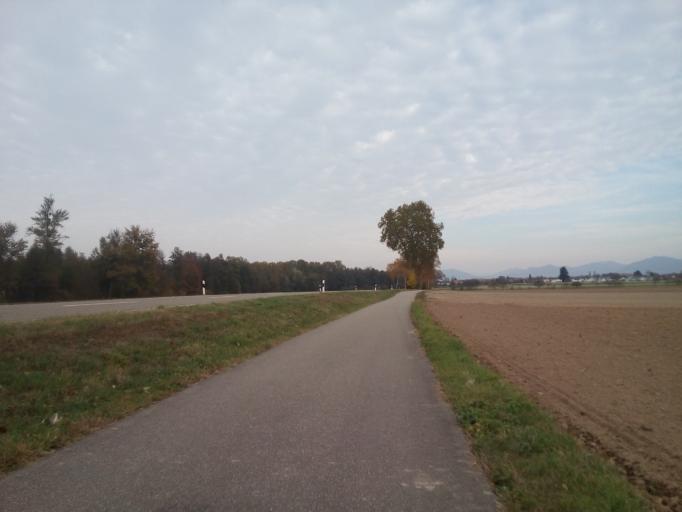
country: DE
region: Baden-Wuerttemberg
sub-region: Karlsruhe Region
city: Zell
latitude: 48.6828
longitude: 8.0415
